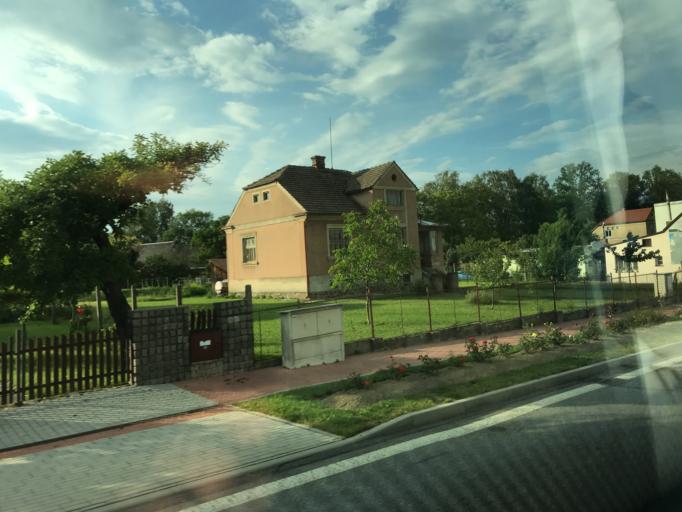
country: CZ
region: Jihocesky
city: Lisov
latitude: 49.0128
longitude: 14.5957
